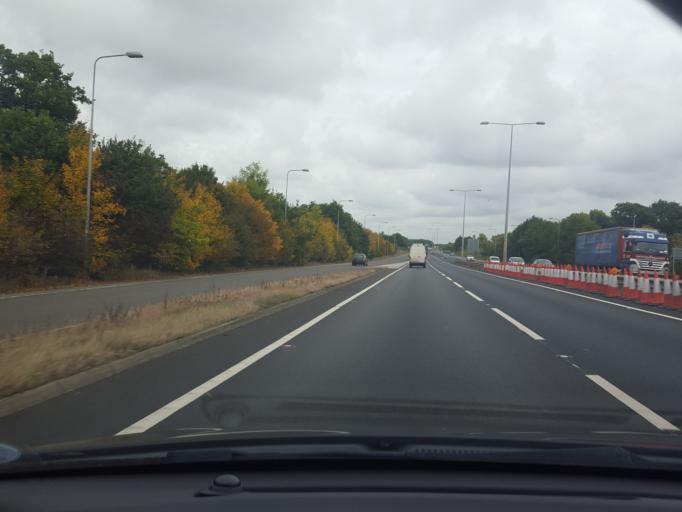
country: GB
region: England
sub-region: Suffolk
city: Capel Saint Mary
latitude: 52.0167
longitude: 1.0733
